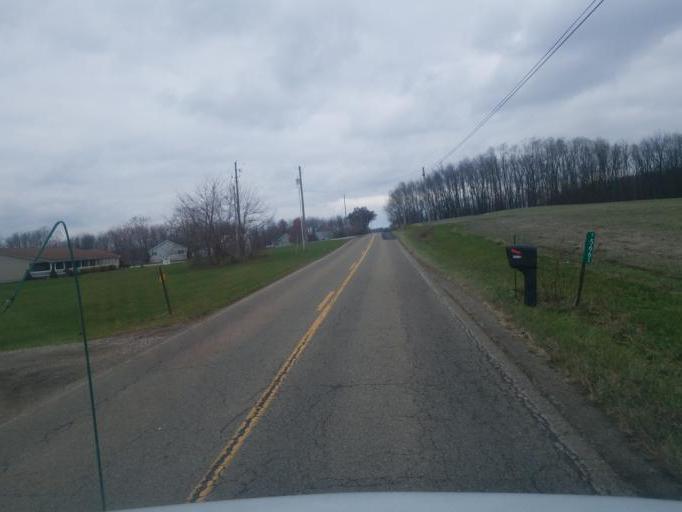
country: US
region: Ohio
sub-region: Knox County
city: Fredericktown
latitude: 40.4640
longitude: -82.5239
